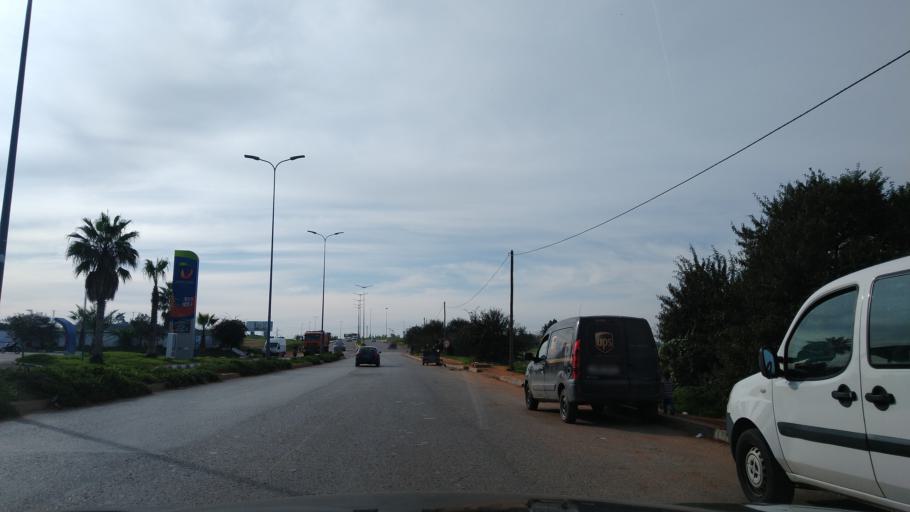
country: MA
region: Rabat-Sale-Zemmour-Zaer
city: Sale
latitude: 33.9874
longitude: -6.7394
